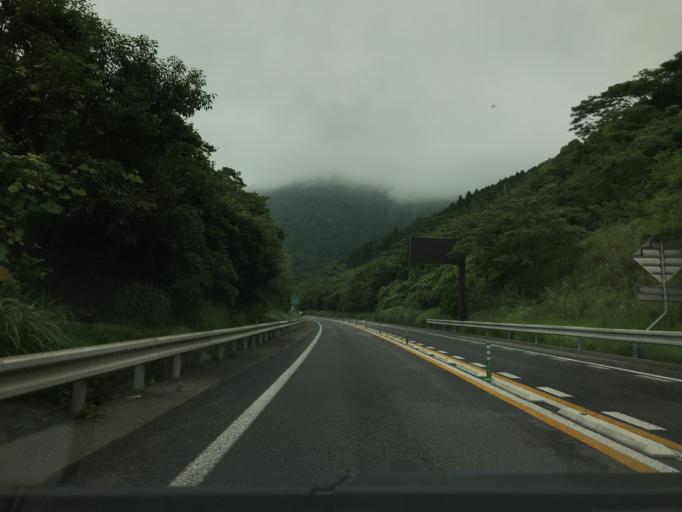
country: JP
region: Oita
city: Bungo-Takada-shi
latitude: 33.4931
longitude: 131.3202
